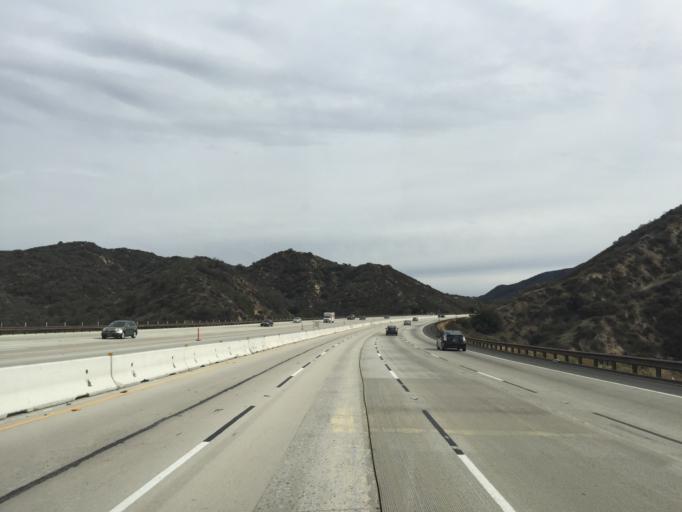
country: US
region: California
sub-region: Los Angeles County
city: Burbank
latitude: 34.2417
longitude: -118.3126
